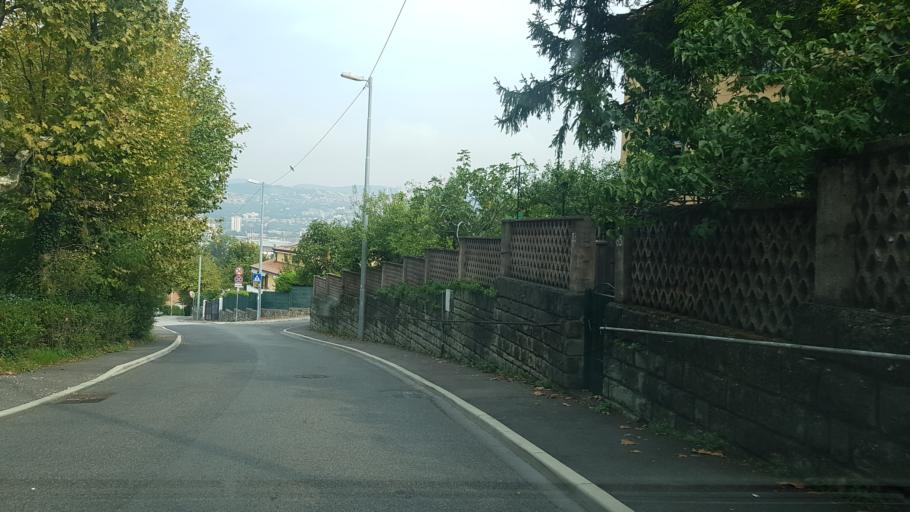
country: IT
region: Friuli Venezia Giulia
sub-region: Provincia di Trieste
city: Domio
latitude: 45.6025
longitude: 13.8063
